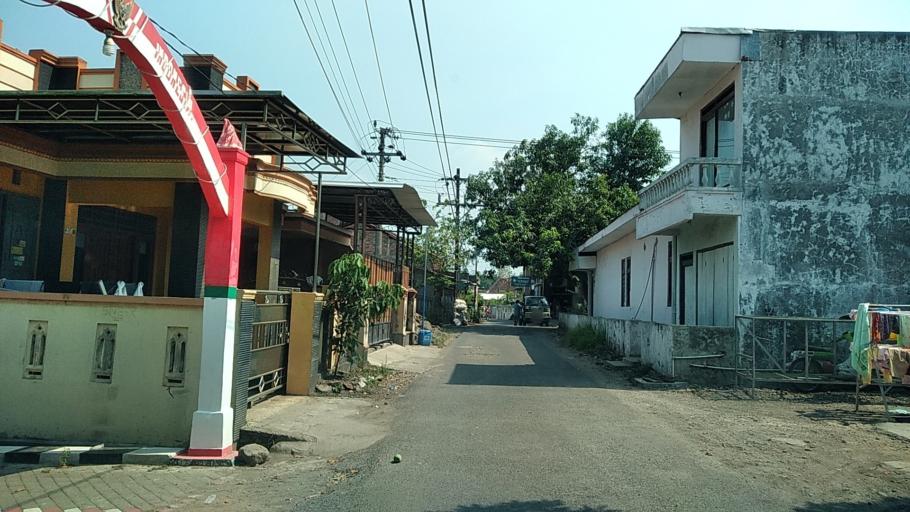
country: ID
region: Central Java
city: Mranggen
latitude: -7.0531
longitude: 110.4800
